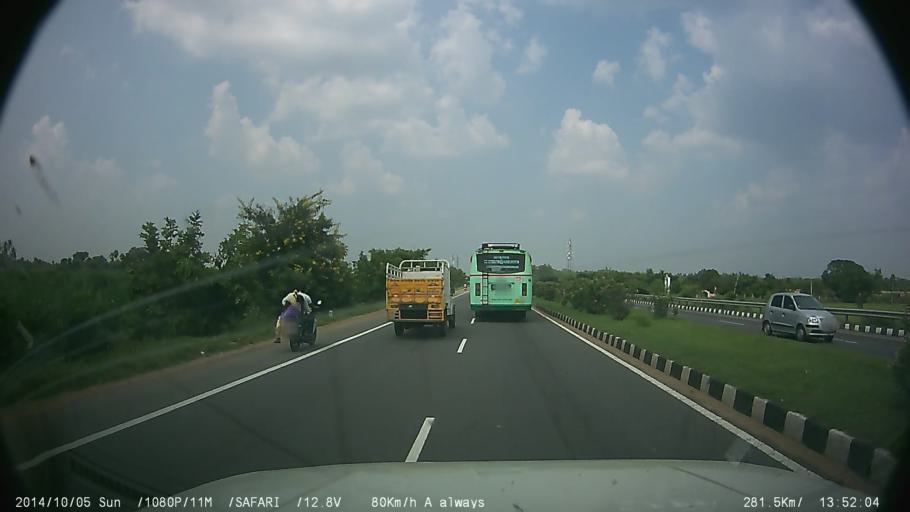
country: IN
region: Tamil Nadu
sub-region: Villupuram
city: Vikravandi
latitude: 12.0889
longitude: 79.5595
